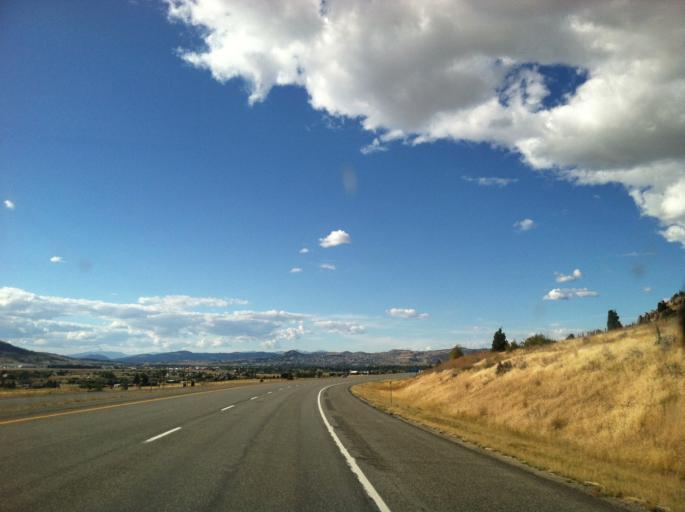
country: US
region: Montana
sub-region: Silver Bow County
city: Butte
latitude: 45.9441
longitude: -112.4626
